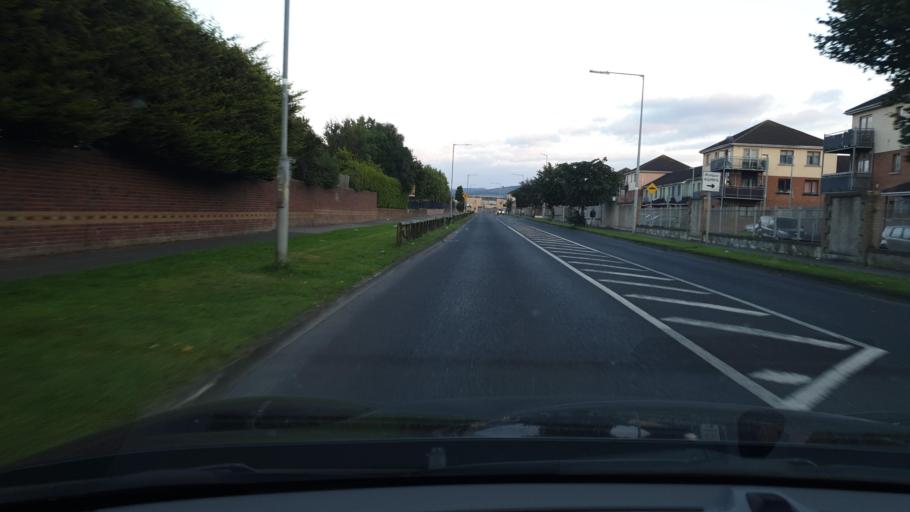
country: IE
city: Jobstown
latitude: 53.2848
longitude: -6.4056
